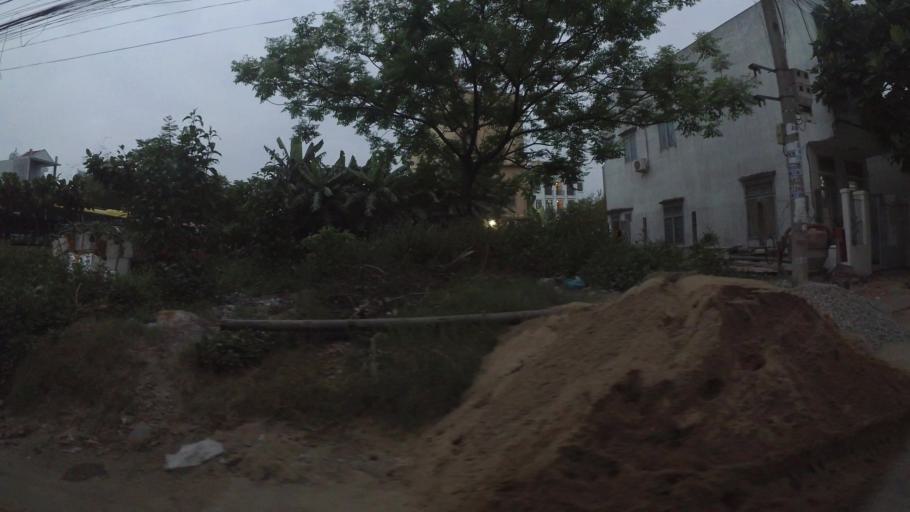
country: VN
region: Da Nang
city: Lien Chieu
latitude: 16.0552
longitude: 108.1711
